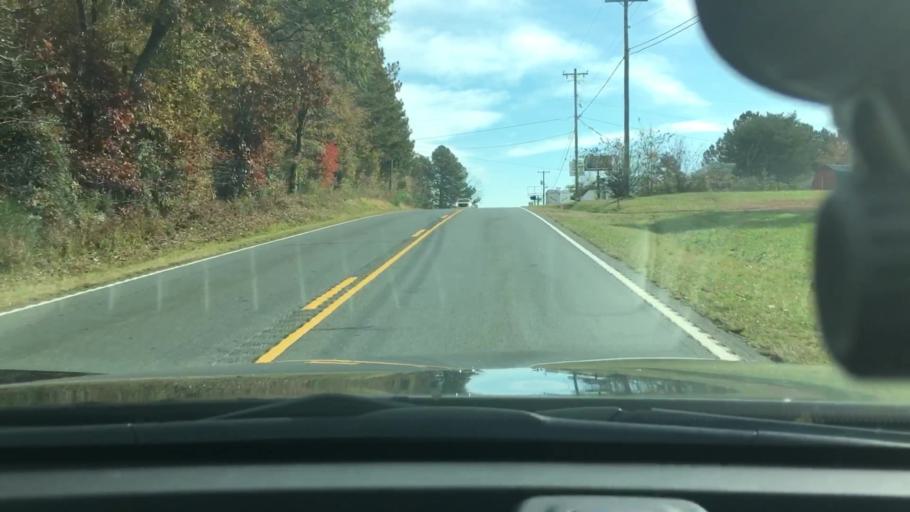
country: US
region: North Carolina
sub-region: Stanly County
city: Badin
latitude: 35.3153
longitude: -80.1045
